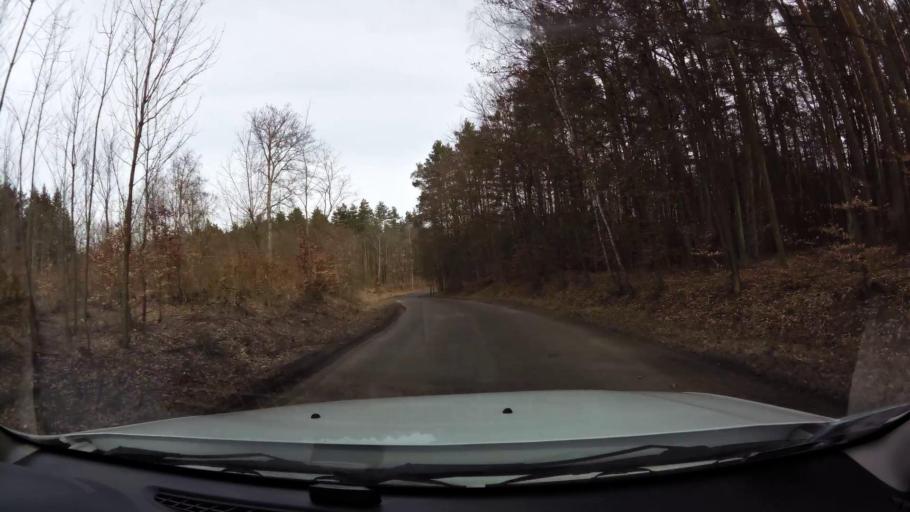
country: PL
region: West Pomeranian Voivodeship
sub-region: Powiat stargardzki
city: Insko
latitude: 53.4564
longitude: 15.6570
